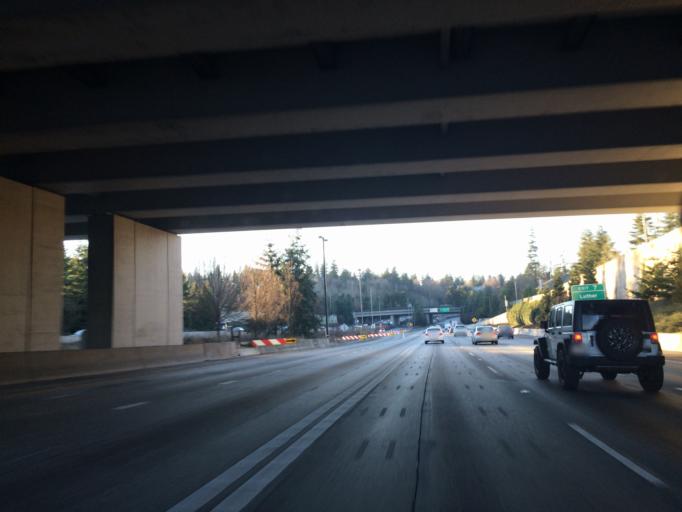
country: US
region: Washington
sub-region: King County
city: Mercer Island
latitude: 47.5782
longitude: -122.2061
